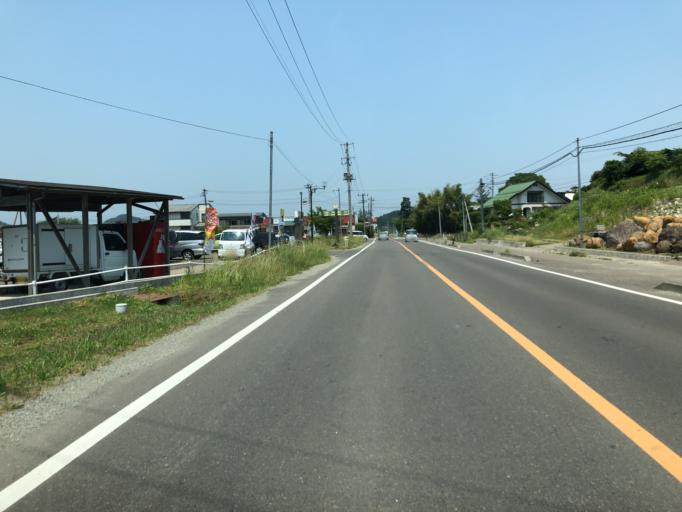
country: JP
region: Miyagi
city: Marumori
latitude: 37.8735
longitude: 140.8237
